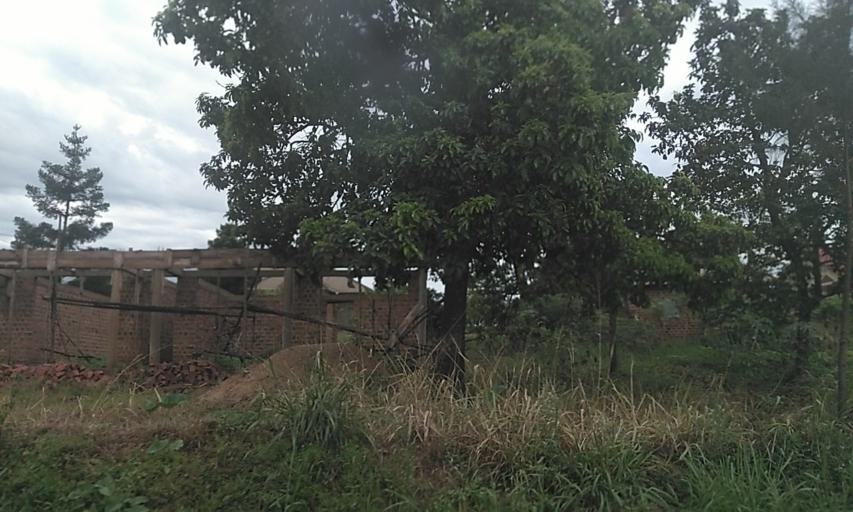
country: UG
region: Central Region
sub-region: Wakiso District
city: Bweyogerere
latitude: 0.3950
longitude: 32.6933
